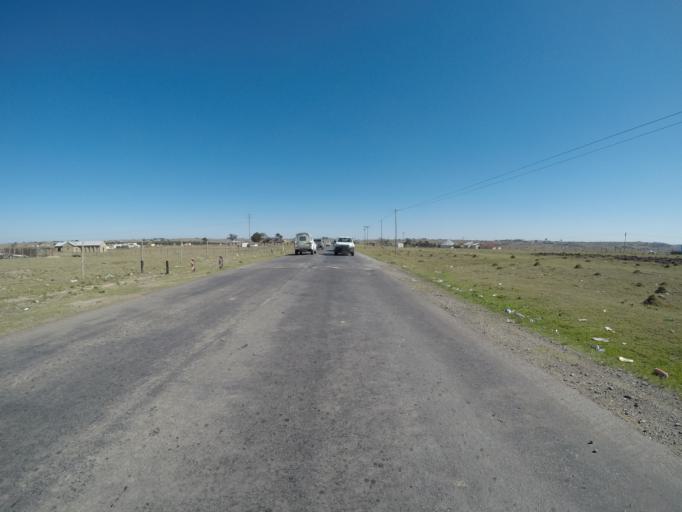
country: ZA
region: Eastern Cape
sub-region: OR Tambo District Municipality
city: Mthatha
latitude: -31.7862
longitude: 28.7421
